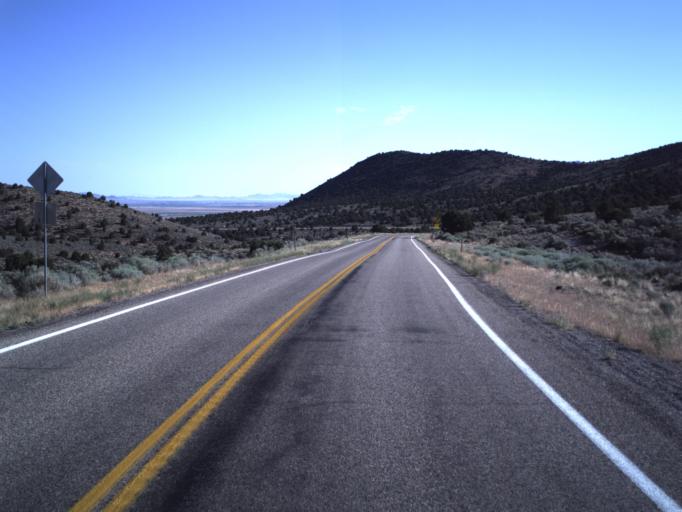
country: US
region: Utah
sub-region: Beaver County
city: Milford
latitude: 38.1150
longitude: -112.9522
